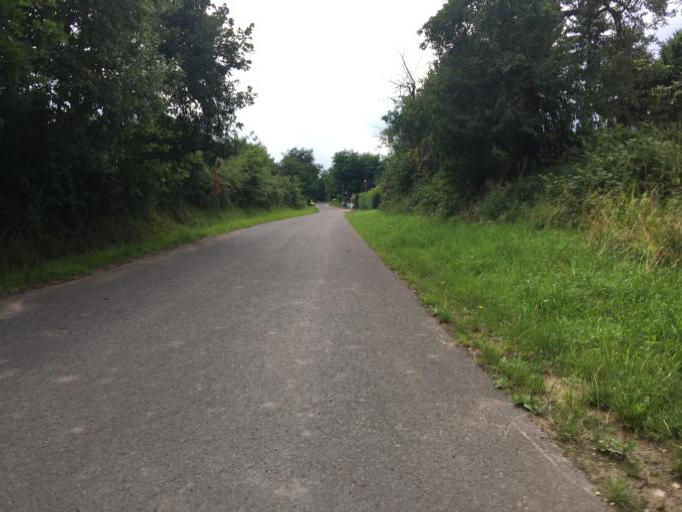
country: DE
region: Hesse
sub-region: Regierungsbezirk Darmstadt
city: Gelnhausen
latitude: 50.1923
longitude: 9.2034
